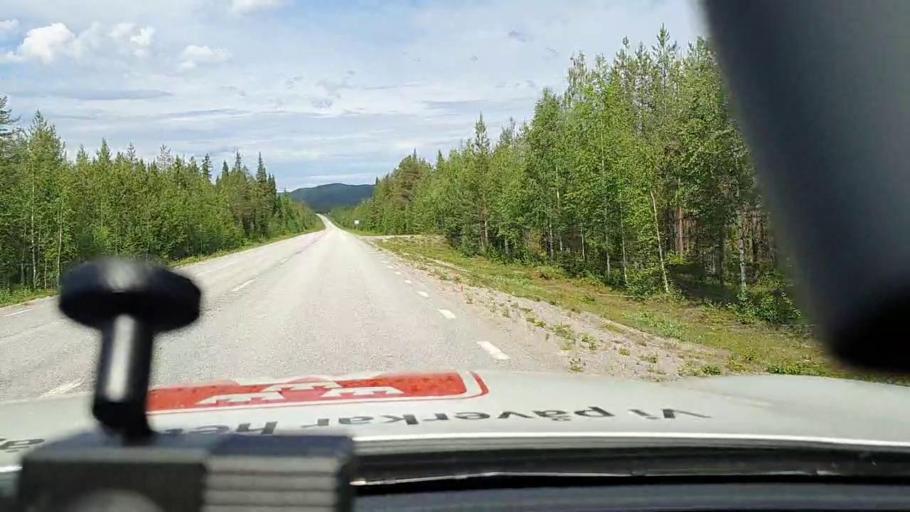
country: SE
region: Norrbotten
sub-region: Jokkmokks Kommun
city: Jokkmokk
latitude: 66.5448
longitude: 20.1363
